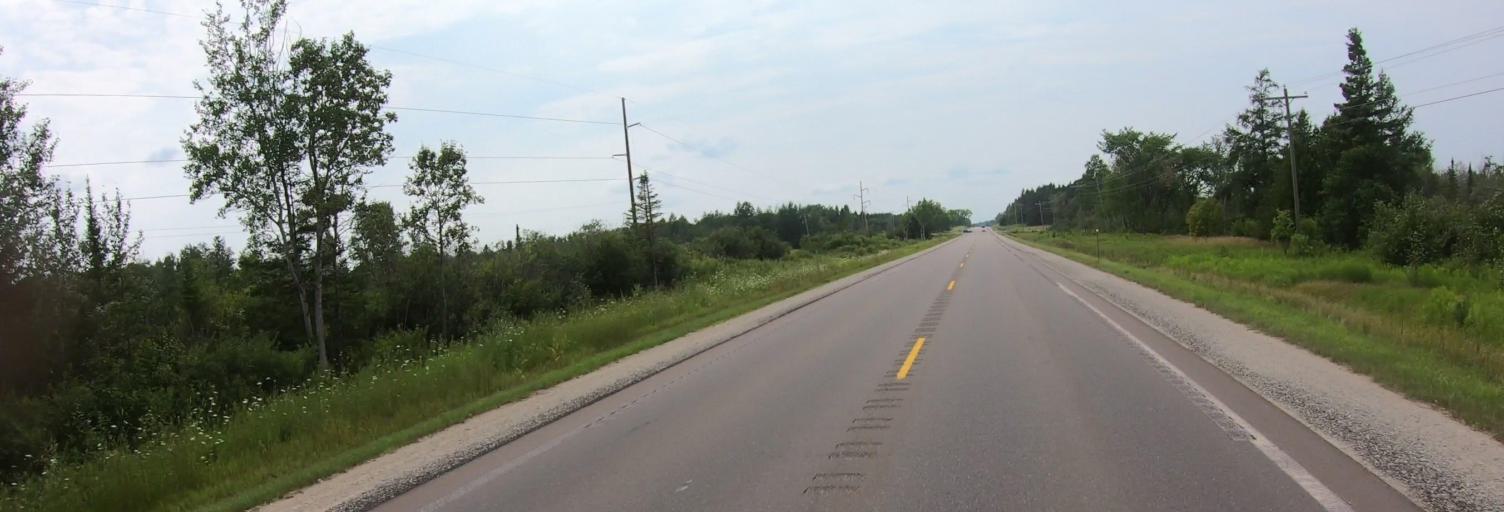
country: US
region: Michigan
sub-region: Alger County
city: Munising
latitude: 46.3527
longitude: -87.0080
